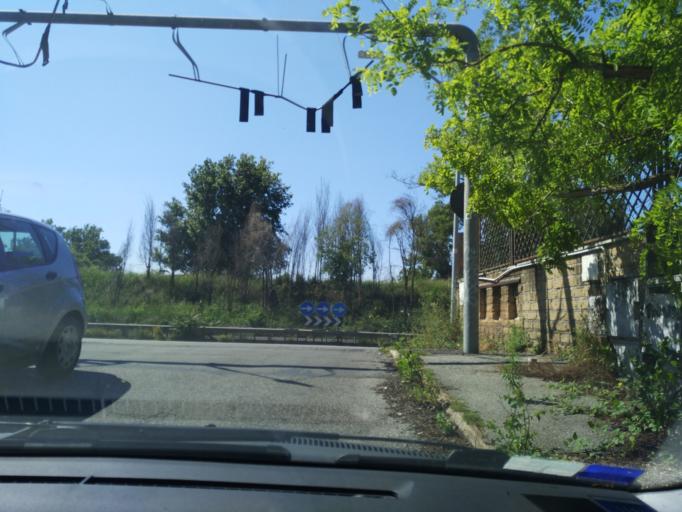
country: IT
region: Latium
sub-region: Citta metropolitana di Roma Capitale
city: Vitinia
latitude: 41.8328
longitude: 12.4542
